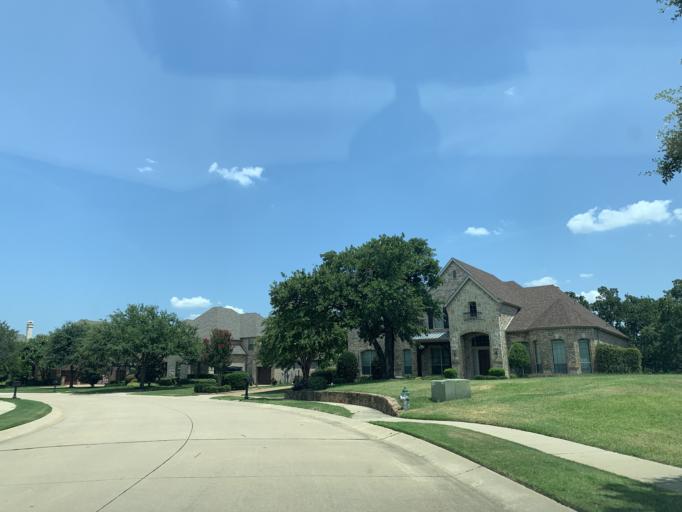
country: US
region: Texas
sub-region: Tarrant County
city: Southlake
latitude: 32.9712
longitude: -97.1519
